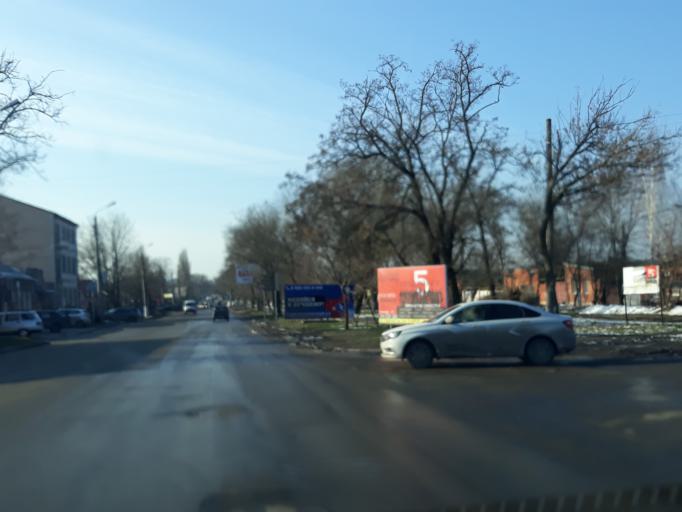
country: RU
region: Rostov
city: Taganrog
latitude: 47.2164
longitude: 38.9134
